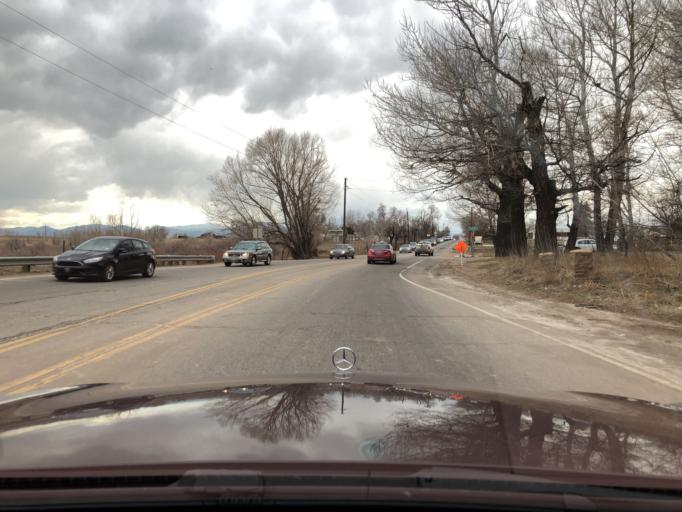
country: US
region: Colorado
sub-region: Boulder County
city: Lafayette
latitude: 40.0149
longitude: -105.1036
